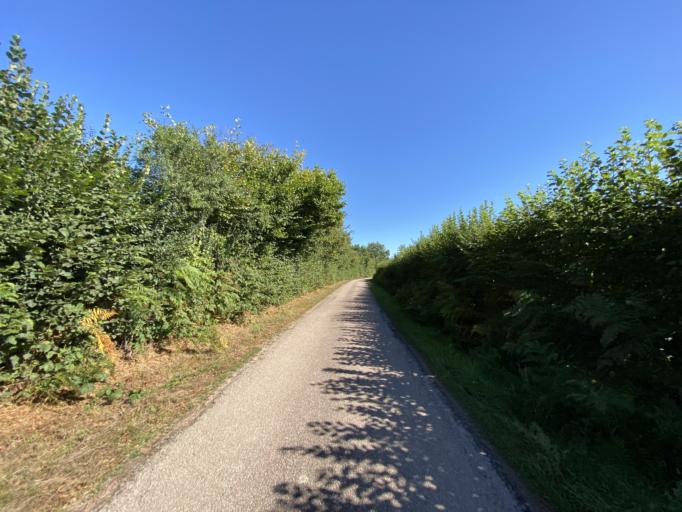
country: FR
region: Bourgogne
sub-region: Departement de la Cote-d'Or
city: Saulieu
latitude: 47.2797
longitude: 4.1797
